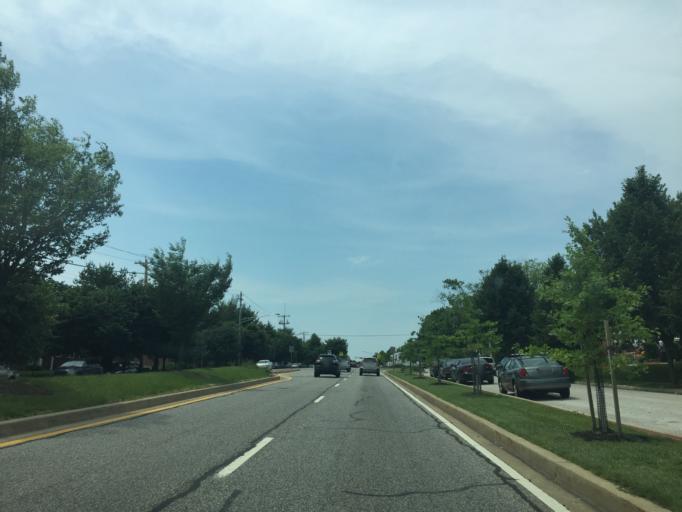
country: US
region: Maryland
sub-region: Baltimore County
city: Parkville
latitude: 39.3894
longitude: -76.5702
